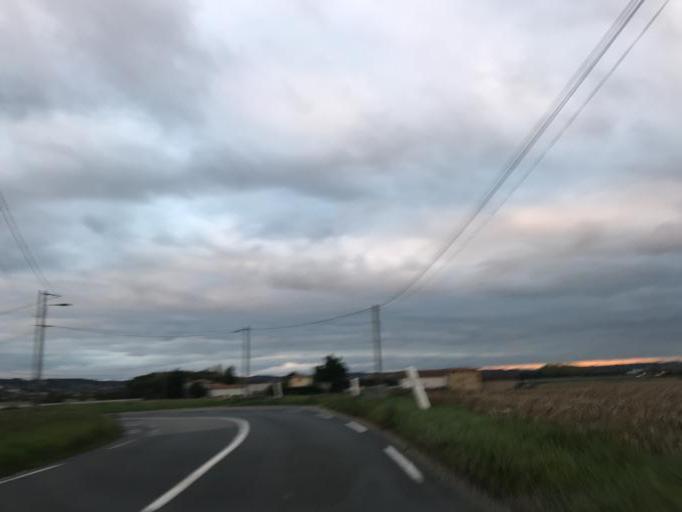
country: FR
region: Rhone-Alpes
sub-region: Departement de l'Ain
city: Trevoux
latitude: 45.9225
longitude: 4.7575
